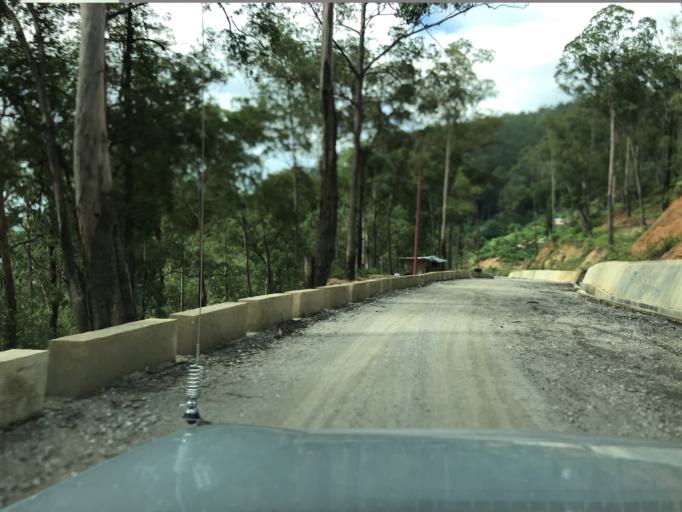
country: TL
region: Aileu
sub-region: Aileu Villa
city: Aileu
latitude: -8.6626
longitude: 125.5315
